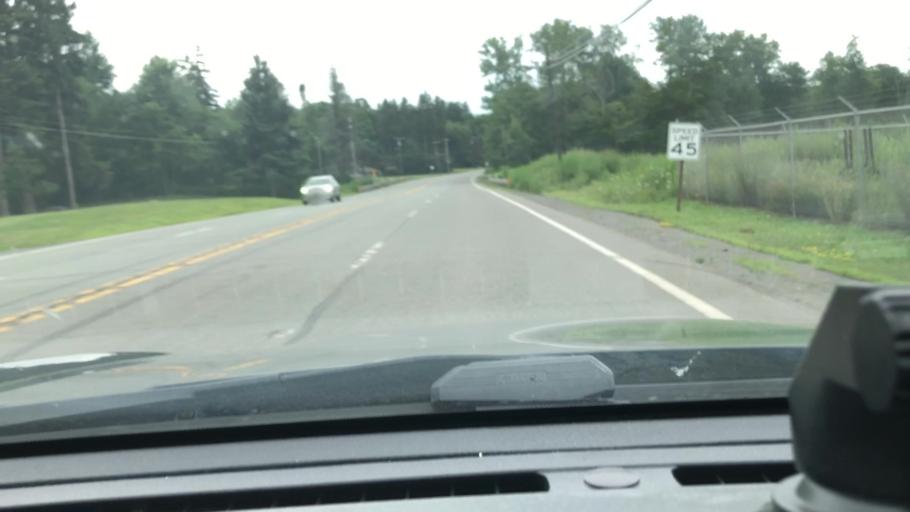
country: US
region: Pennsylvania
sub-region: Lackawanna County
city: Moscow
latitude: 41.2472
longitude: -75.5027
